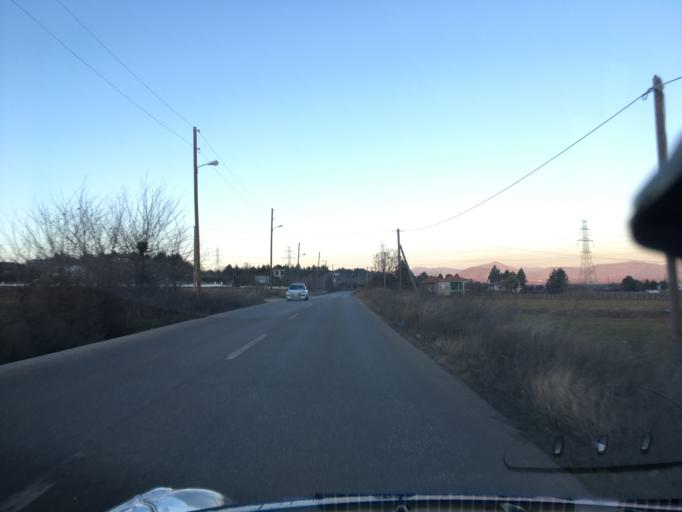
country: GR
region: West Macedonia
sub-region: Nomos Kozanis
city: Kozani
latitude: 40.2590
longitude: 21.7601
